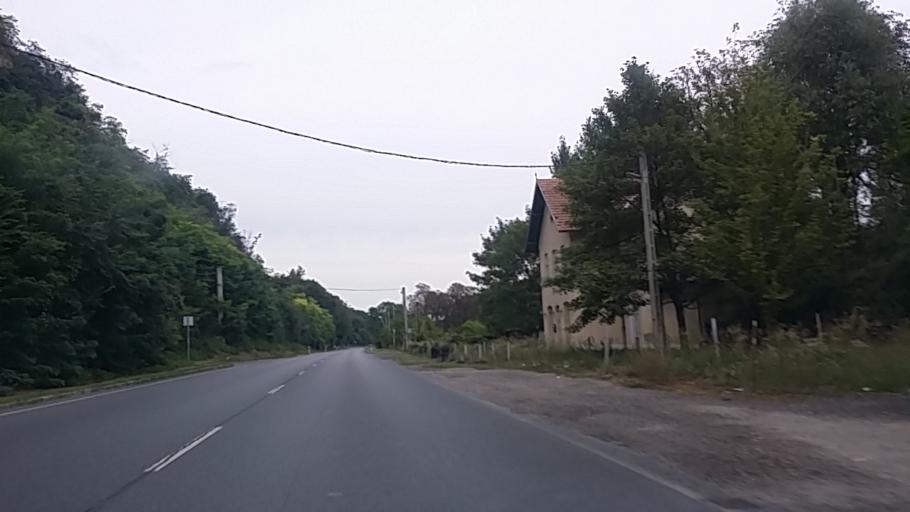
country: HU
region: Tolna
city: Paks
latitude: 46.6408
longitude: 18.8786
